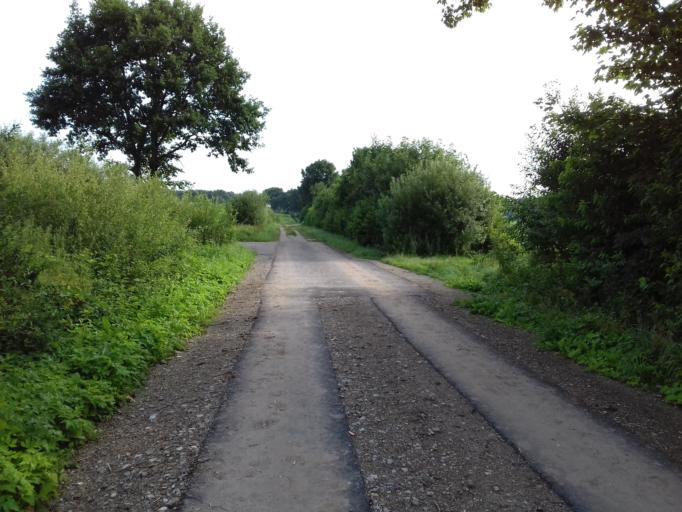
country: DE
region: Schleswig-Holstein
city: Bonebuttel
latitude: 54.0815
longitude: 10.0471
